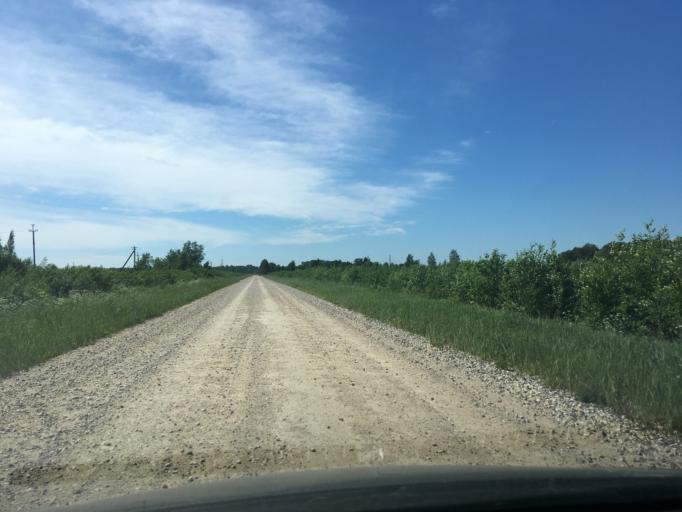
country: EE
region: Paernumaa
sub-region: Audru vald
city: Audru
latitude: 58.4686
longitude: 24.3974
